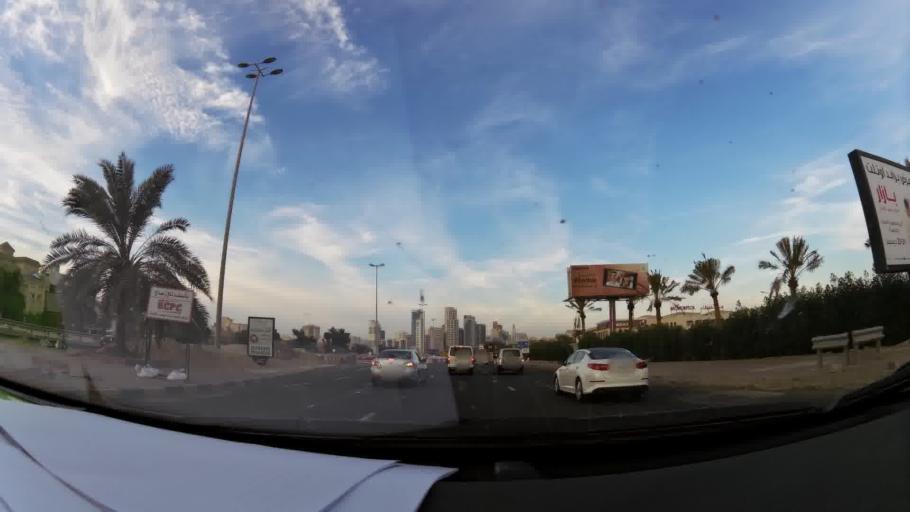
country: KW
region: Muhafazat Hawalli
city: Ar Rumaythiyah
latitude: 29.3175
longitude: 48.0876
